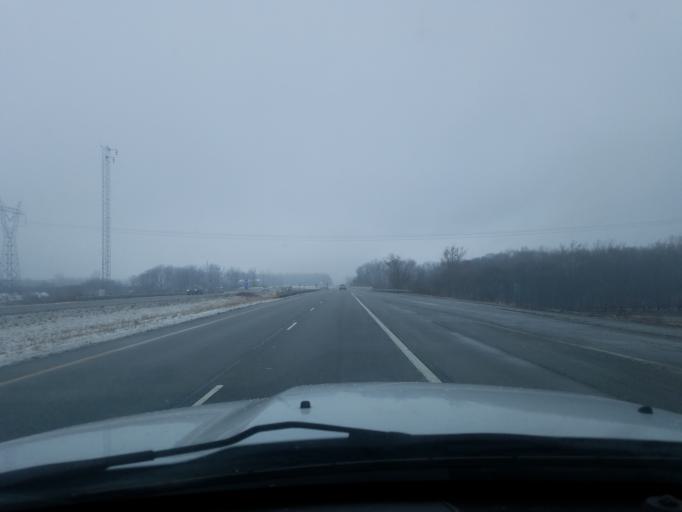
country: US
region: Indiana
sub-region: Hamilton County
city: Westfield
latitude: 40.0925
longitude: -86.1277
